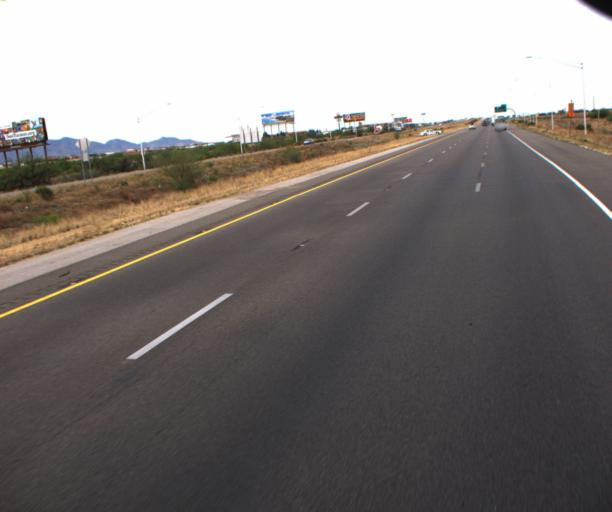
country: US
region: Arizona
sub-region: Cochise County
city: Whetstone
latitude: 31.9673
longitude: -110.3370
